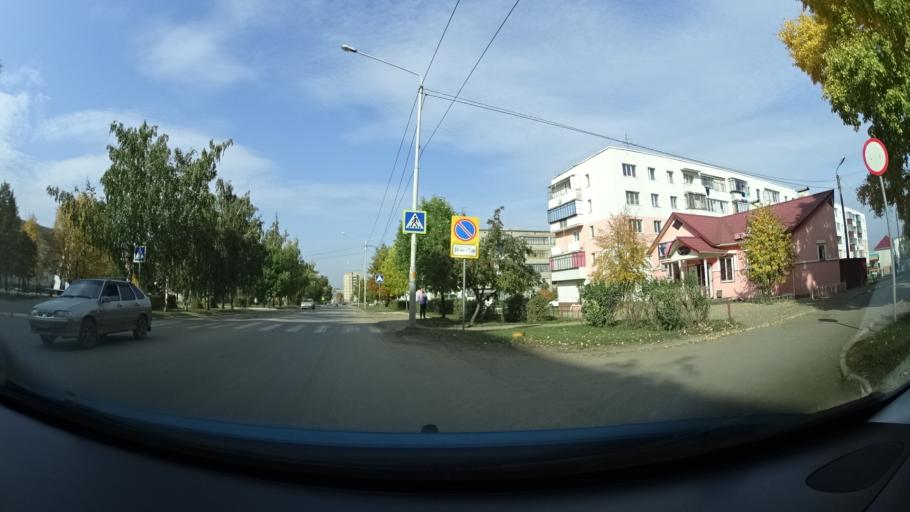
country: RU
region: Bashkortostan
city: Tuymazy
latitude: 54.6043
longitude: 53.6977
